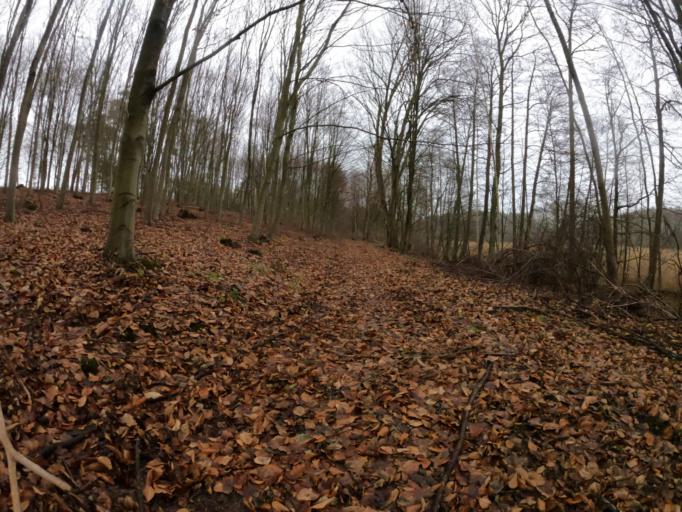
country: PL
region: West Pomeranian Voivodeship
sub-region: Powiat mysliborski
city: Debno
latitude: 52.7519
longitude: 14.7706
